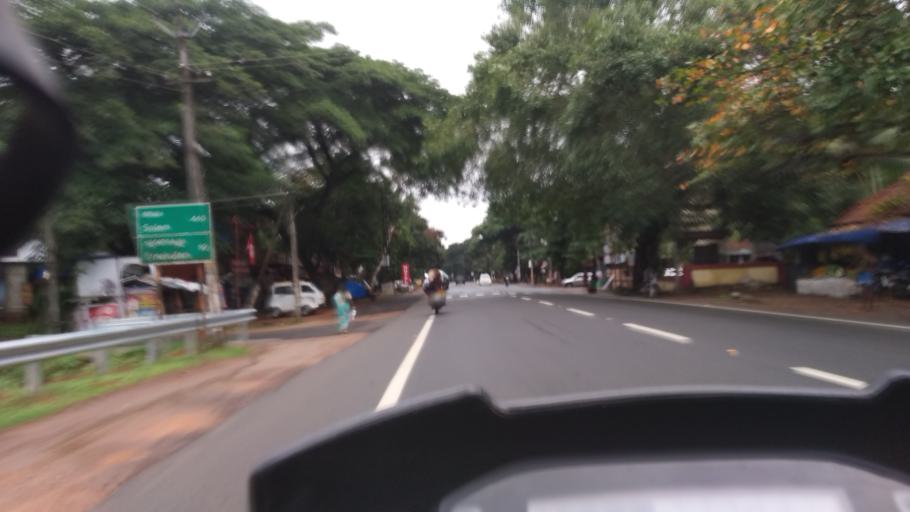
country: IN
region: Kerala
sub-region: Alappuzha
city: Mavelikara
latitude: 9.3064
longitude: 76.4320
